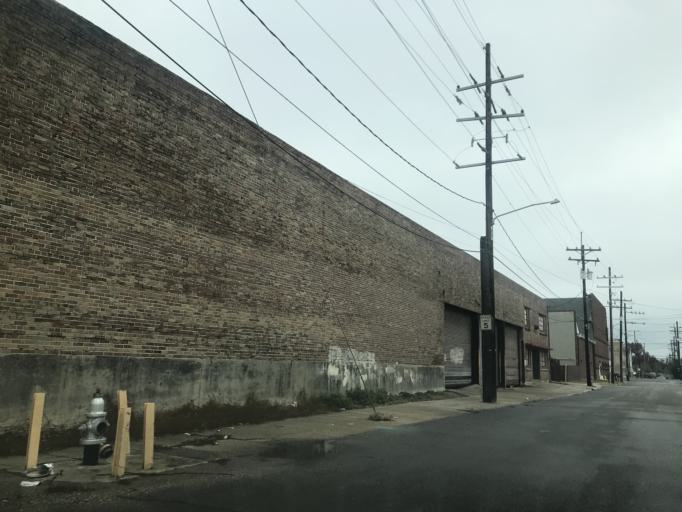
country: US
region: Louisiana
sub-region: Orleans Parish
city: New Orleans
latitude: 29.9666
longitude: -90.1044
